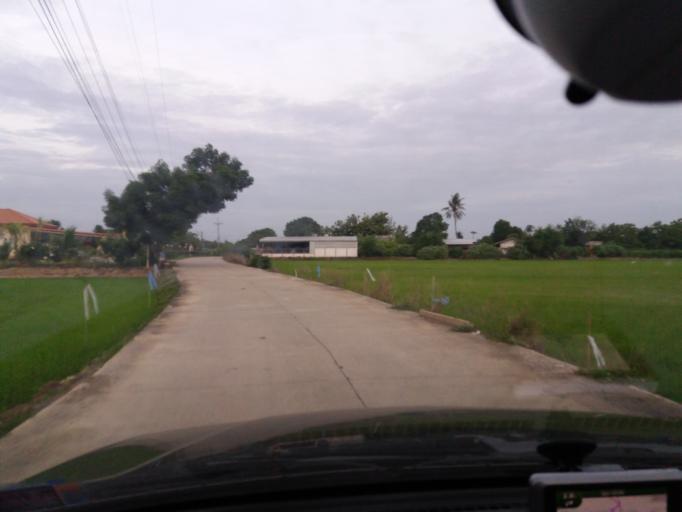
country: TH
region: Suphan Buri
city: Ban Sam Chuk
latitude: 14.7169
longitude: 100.0560
